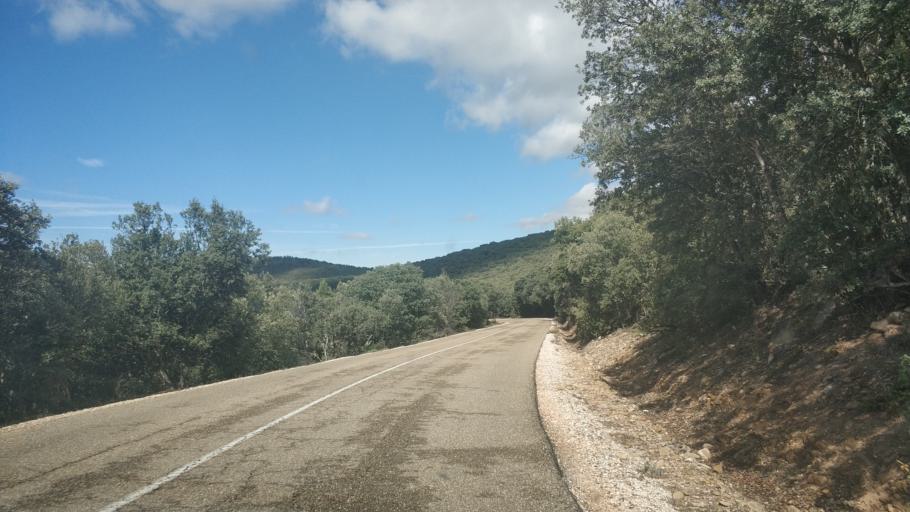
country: ES
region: Castille and Leon
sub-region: Provincia de Burgos
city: Retuerta
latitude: 42.0371
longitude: -3.4832
